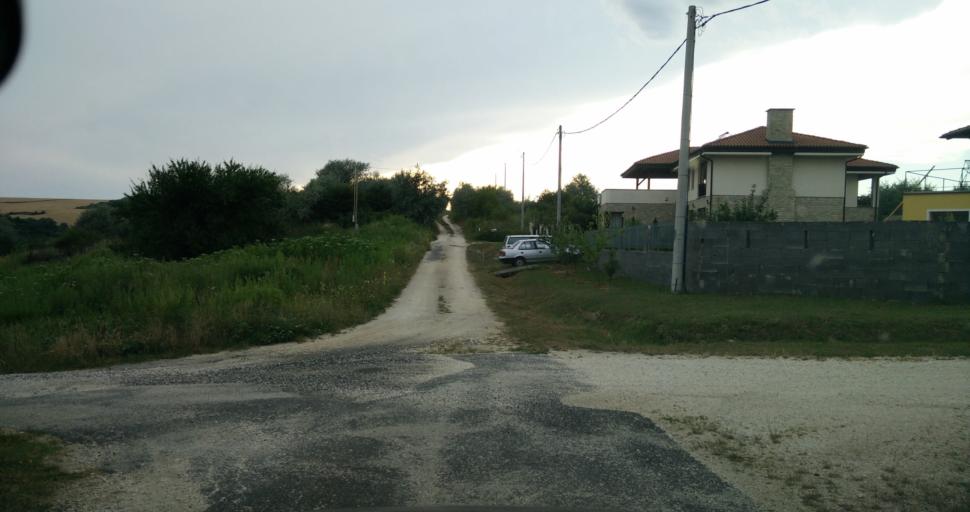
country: HU
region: Pest
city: Piliscsaba
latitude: 47.6421
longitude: 18.7917
